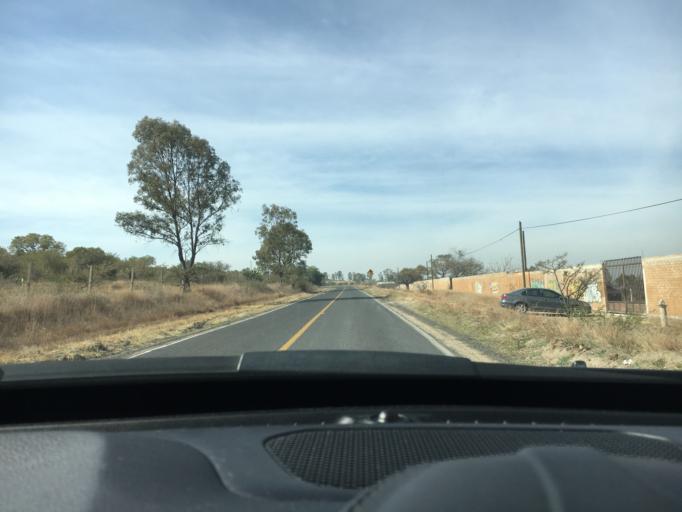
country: MX
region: Guanajuato
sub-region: Silao de la Victoria
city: San Francisco (Banos de Agua Caliente)
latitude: 21.0716
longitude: -101.4928
